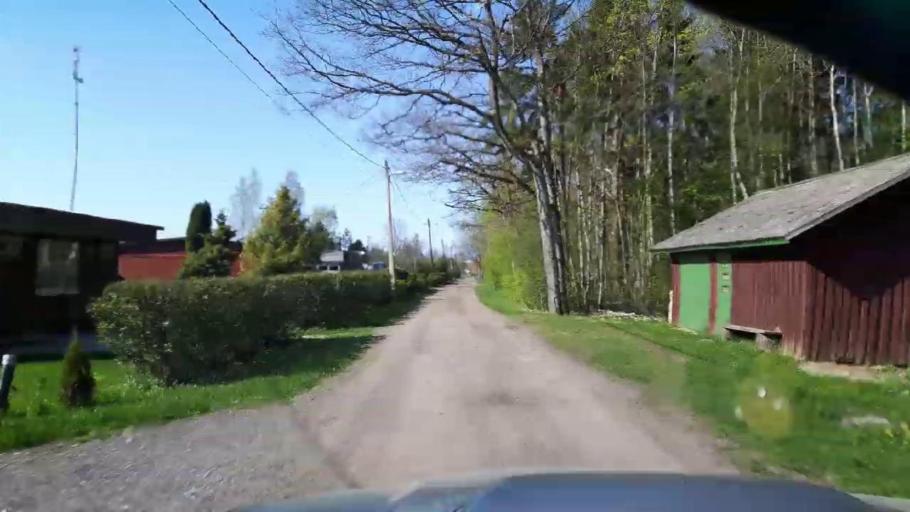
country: EE
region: Paernumaa
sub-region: Sindi linn
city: Sindi
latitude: 58.4509
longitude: 24.7686
